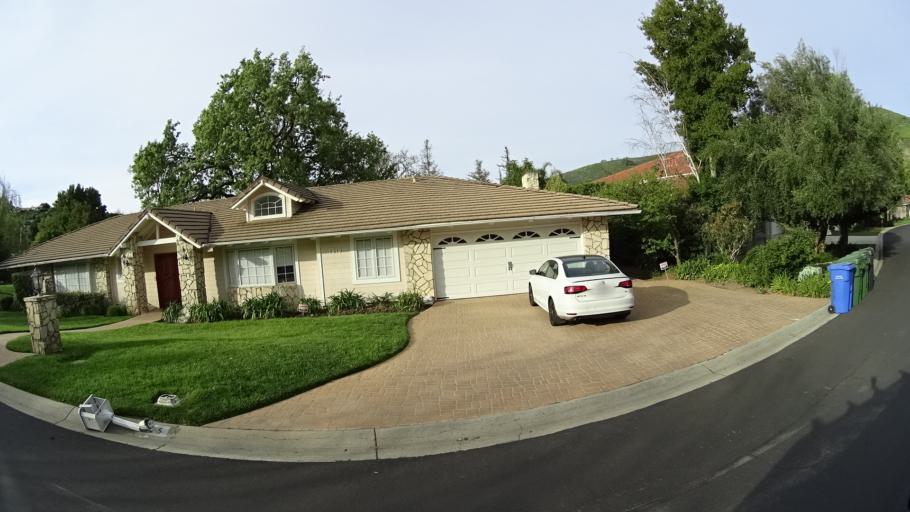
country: US
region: California
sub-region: Ventura County
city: Thousand Oaks
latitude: 34.1911
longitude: -118.8190
